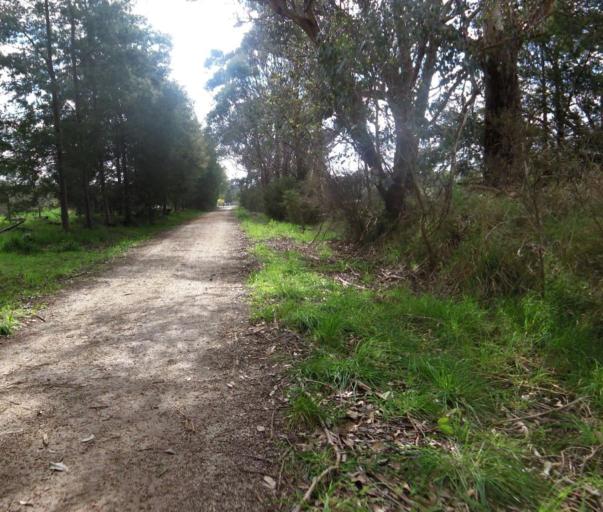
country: AU
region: Victoria
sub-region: Bass Coast
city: North Wonthaggi
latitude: -38.5875
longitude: 146.0381
